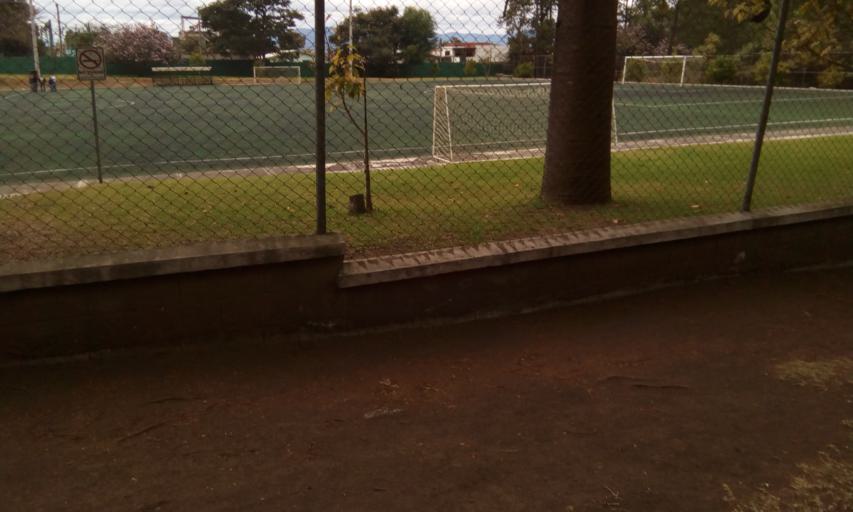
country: GT
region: Guatemala
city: Santa Catarina Pinula
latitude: 14.5984
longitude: -90.4848
